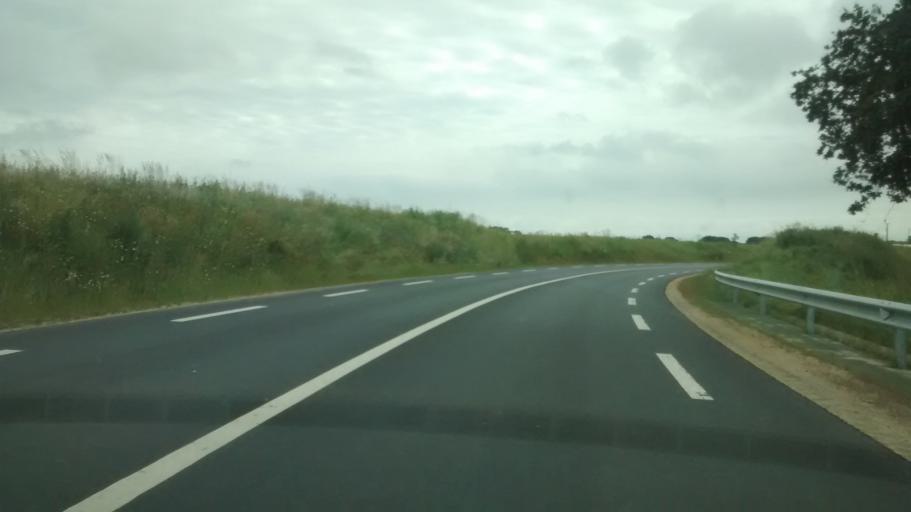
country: FR
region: Brittany
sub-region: Departement du Morbihan
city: Queven
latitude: 47.7747
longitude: -3.4189
